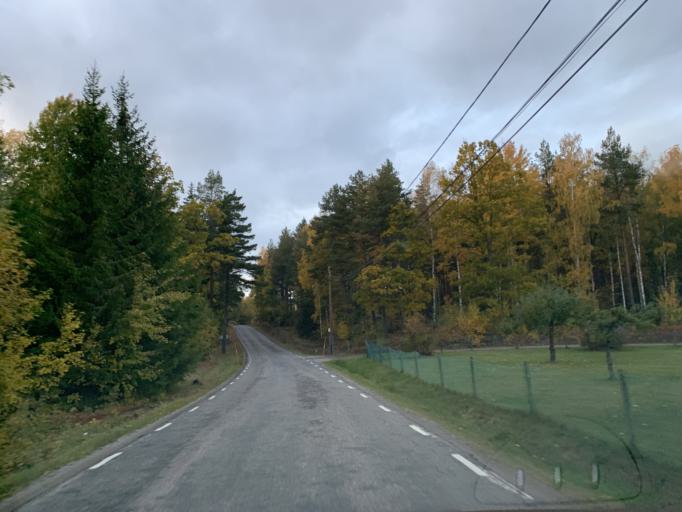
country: SE
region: Stockholm
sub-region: Nynashamns Kommun
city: Osmo
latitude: 58.9172
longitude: 17.7793
